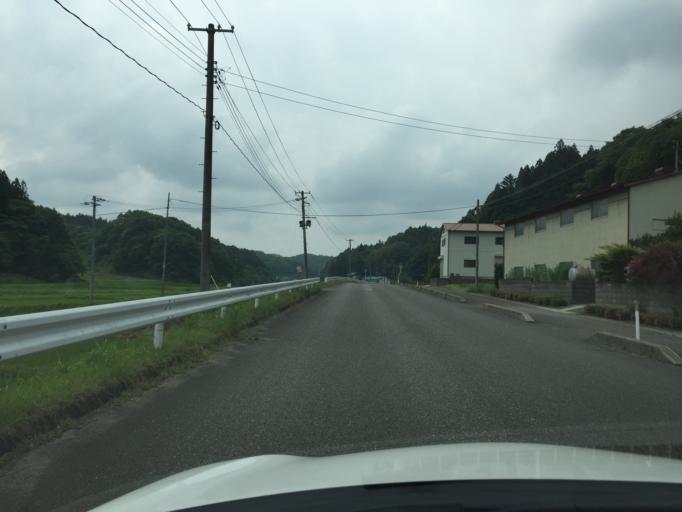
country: JP
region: Fukushima
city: Funehikimachi-funehiki
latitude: 37.2914
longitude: 140.5868
